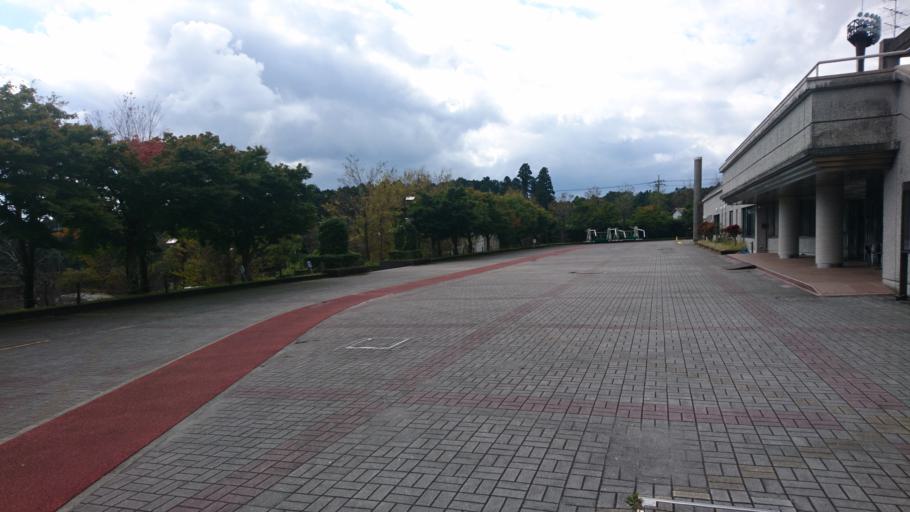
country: JP
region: Shizuoka
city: Gotemba
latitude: 35.3133
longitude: 138.9120
